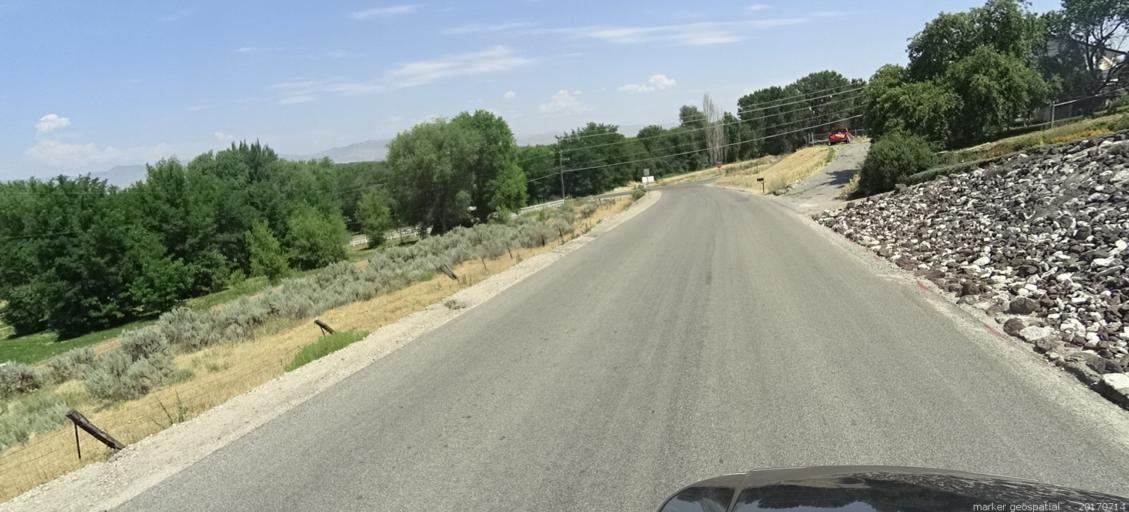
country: US
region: Idaho
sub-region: Ada County
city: Meridian
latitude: 43.5355
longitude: -116.3158
